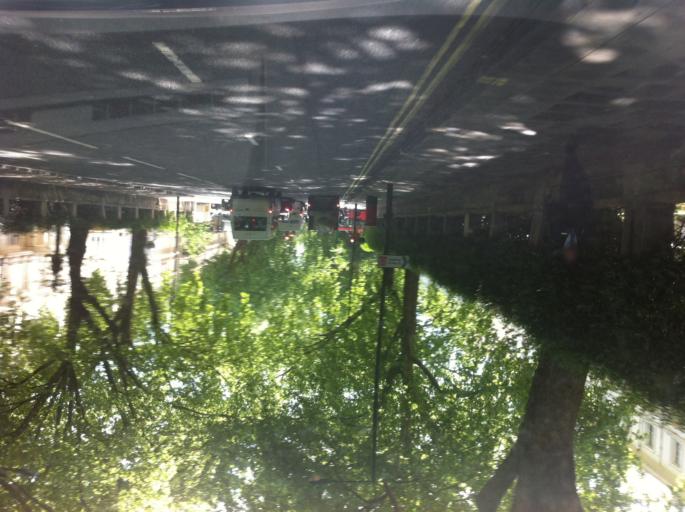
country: GB
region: England
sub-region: Greater London
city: Bayswater
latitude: 51.5151
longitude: -0.1785
